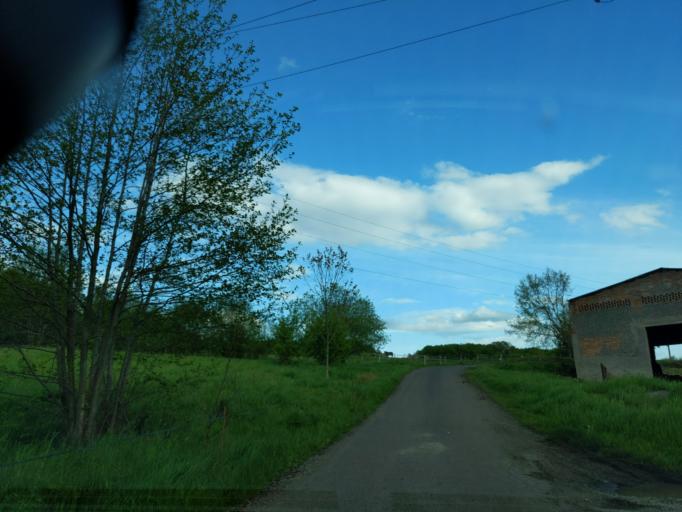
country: CZ
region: Ustecky
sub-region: Okres Usti nad Labem
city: Usti nad Labem
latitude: 50.7124
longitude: 14.0008
